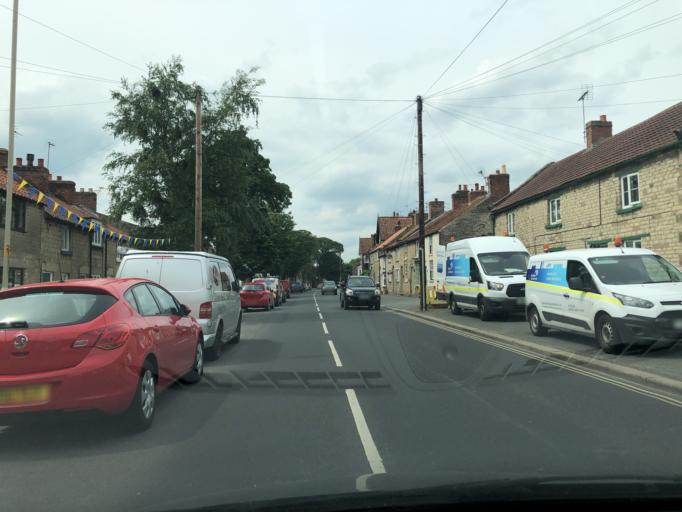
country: GB
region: England
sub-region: North Yorkshire
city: Pickering
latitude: 54.2459
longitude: -0.7848
